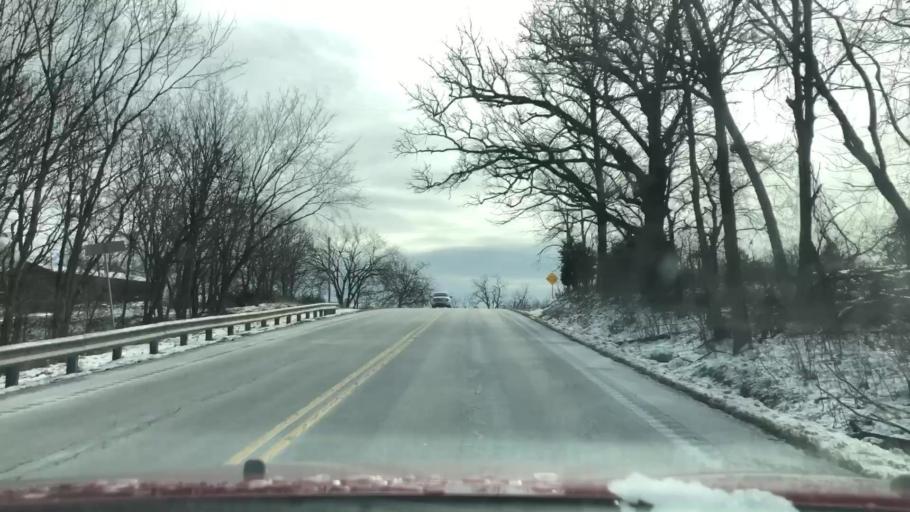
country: US
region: Missouri
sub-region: Jackson County
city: Oak Grove
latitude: 38.9347
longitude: -94.1333
